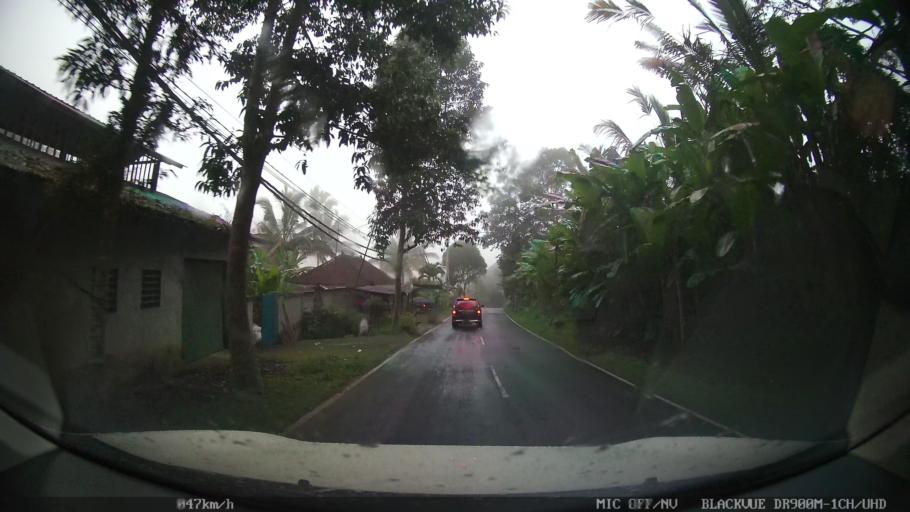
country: ID
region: Bali
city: Banjar Taro Kelod
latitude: -8.3475
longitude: 115.2789
